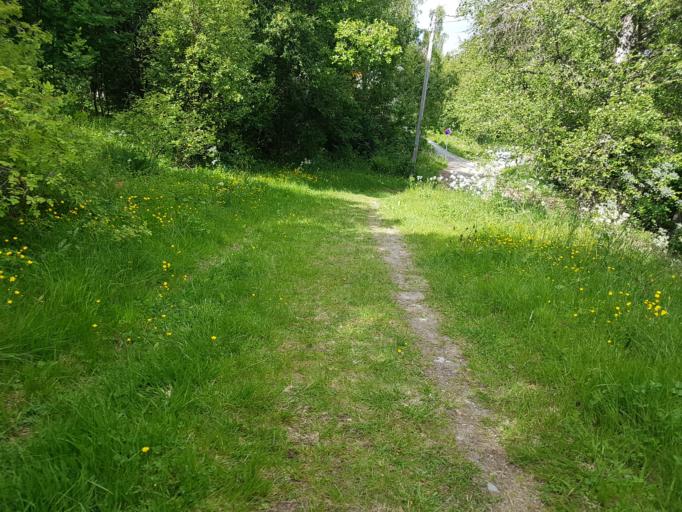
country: NO
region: Sor-Trondelag
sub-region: Trondheim
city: Trondheim
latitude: 63.4022
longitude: 10.3122
